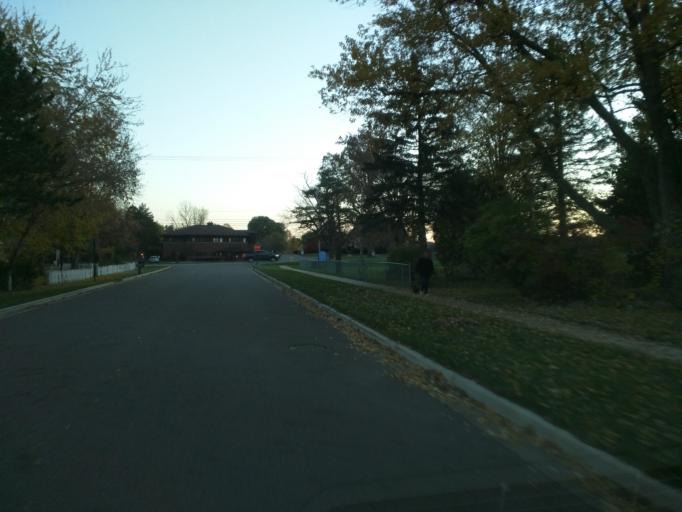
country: US
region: Michigan
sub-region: Eaton County
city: Waverly
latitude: 42.7273
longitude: -84.6104
